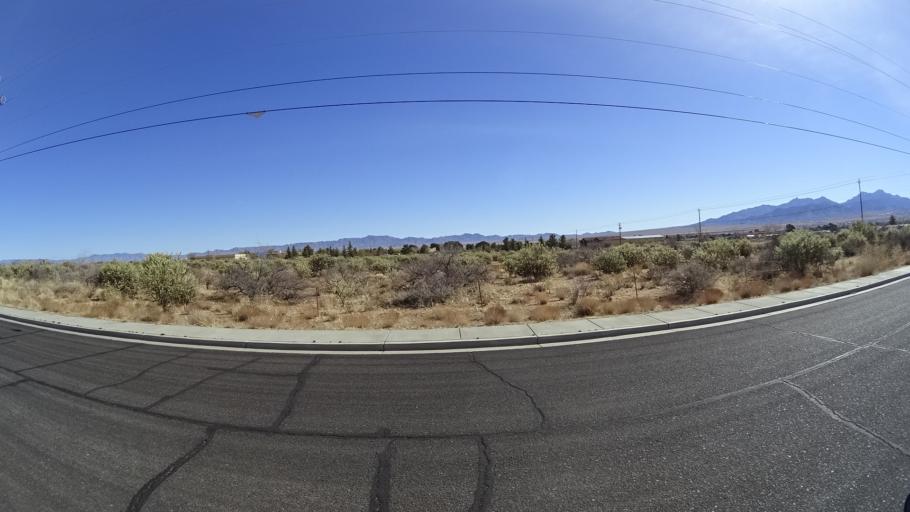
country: US
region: Arizona
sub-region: Mohave County
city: New Kingman-Butler
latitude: 35.2700
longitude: -114.0349
